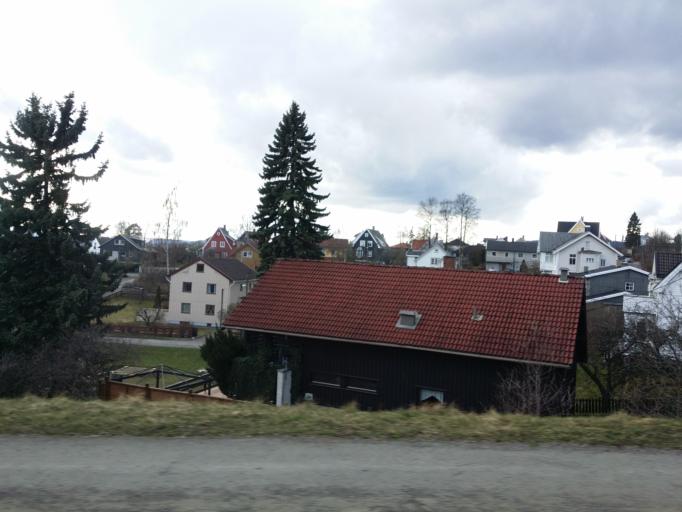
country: NO
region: Oslo
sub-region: Oslo
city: Oslo
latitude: 59.9491
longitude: 10.7900
